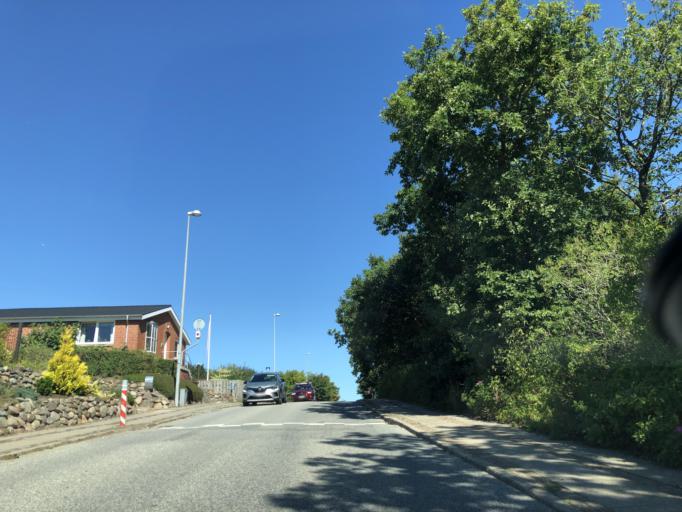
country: DK
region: North Denmark
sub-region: Mariagerfjord Kommune
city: Hobro
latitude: 56.6470
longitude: 9.8006
